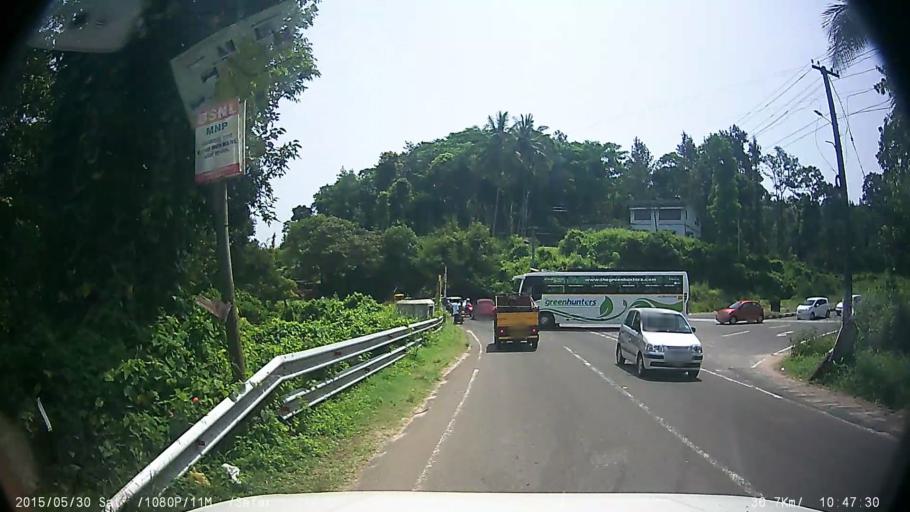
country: IN
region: Kerala
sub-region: Wayanad
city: Kalpetta
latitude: 11.6303
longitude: 76.0894
